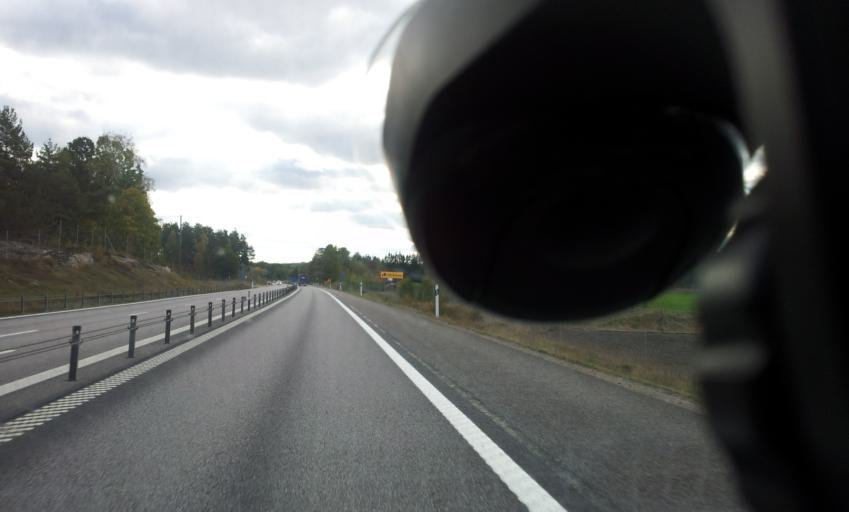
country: SE
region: OEstergoetland
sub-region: Valdemarsviks Kommun
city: Gusum
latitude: 58.3629
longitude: 16.4349
